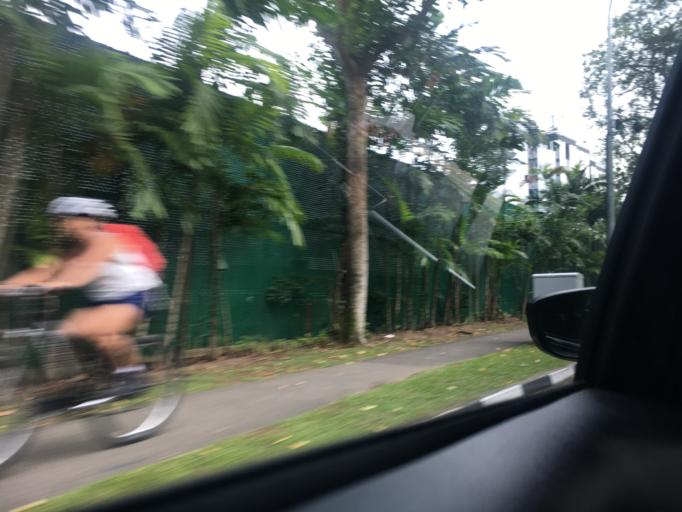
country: SG
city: Singapore
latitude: 1.3078
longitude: 103.8417
